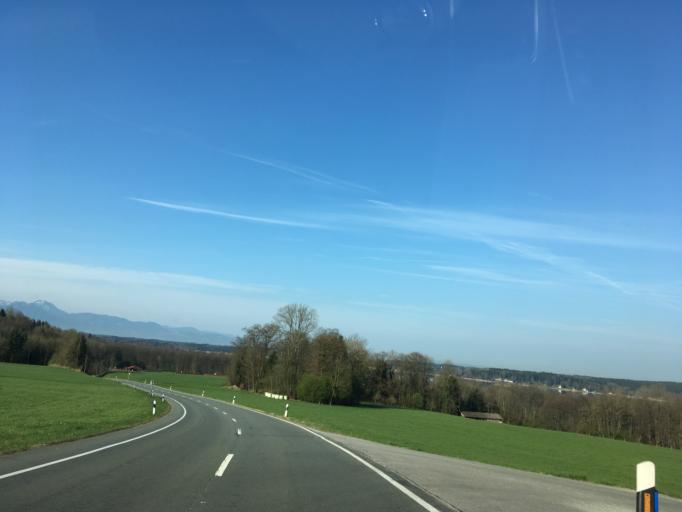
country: DE
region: Bavaria
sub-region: Upper Bavaria
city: Riedering
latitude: 47.8641
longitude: 12.2482
